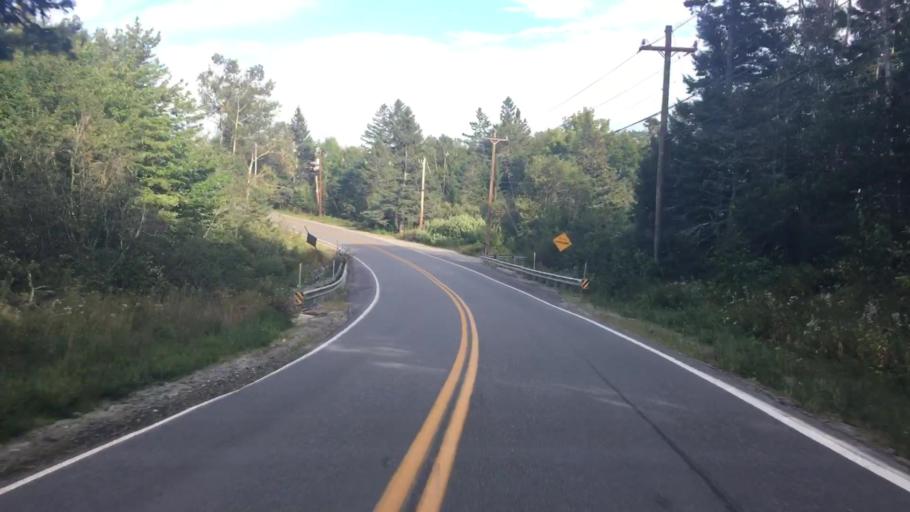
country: US
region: Maine
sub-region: Hancock County
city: Trenton
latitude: 44.4376
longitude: -68.3929
